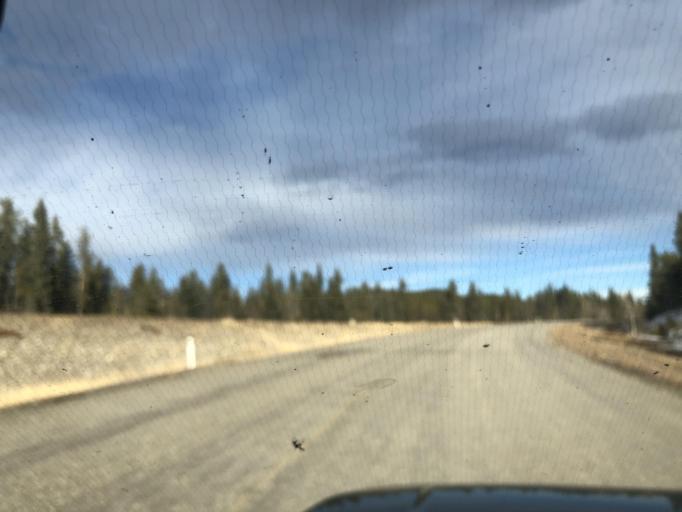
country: CA
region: Alberta
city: Cochrane
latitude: 51.0415
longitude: -114.8655
